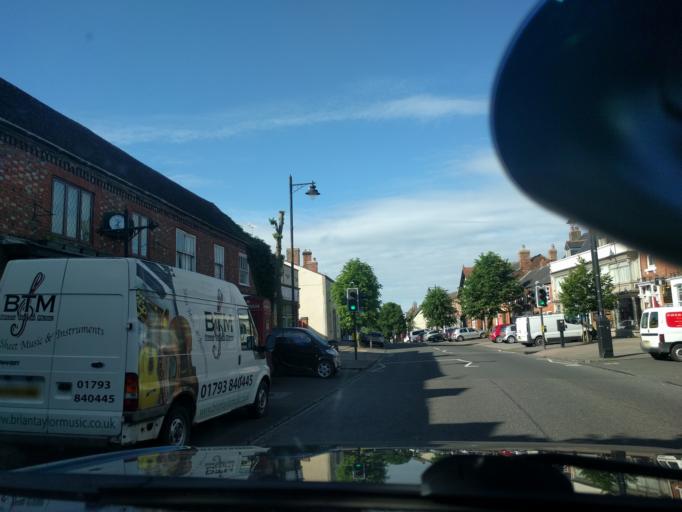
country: GB
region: England
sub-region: Wiltshire
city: Royal Wootton Bassett
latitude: 51.5411
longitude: -1.9056
